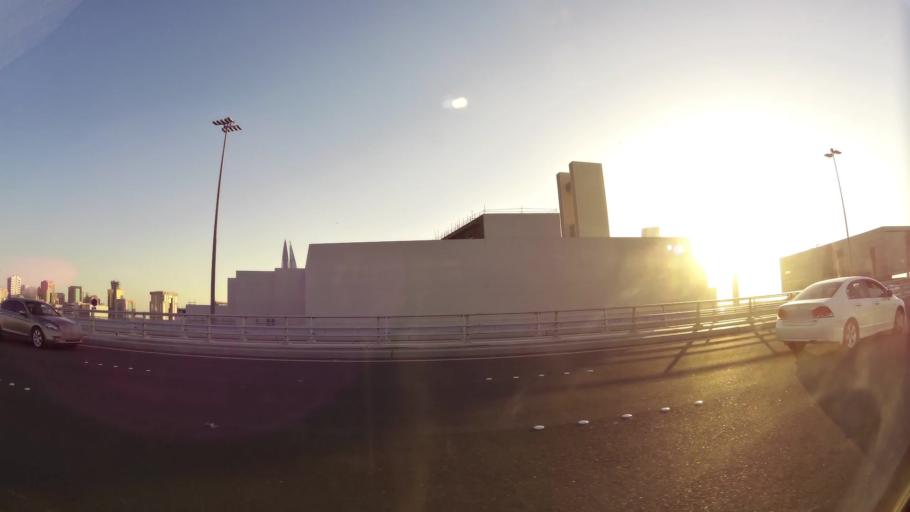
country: BH
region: Muharraq
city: Al Muharraq
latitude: 26.2495
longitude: 50.5865
